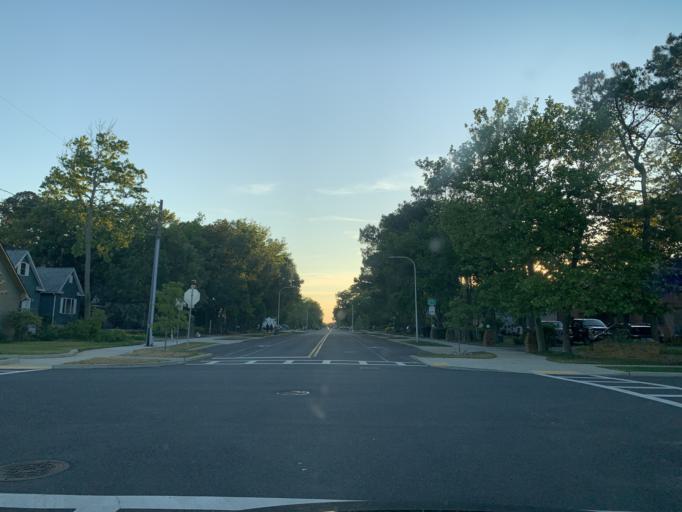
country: US
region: Delaware
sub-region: Sussex County
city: Bethany Beach
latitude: 38.4465
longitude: -75.0542
